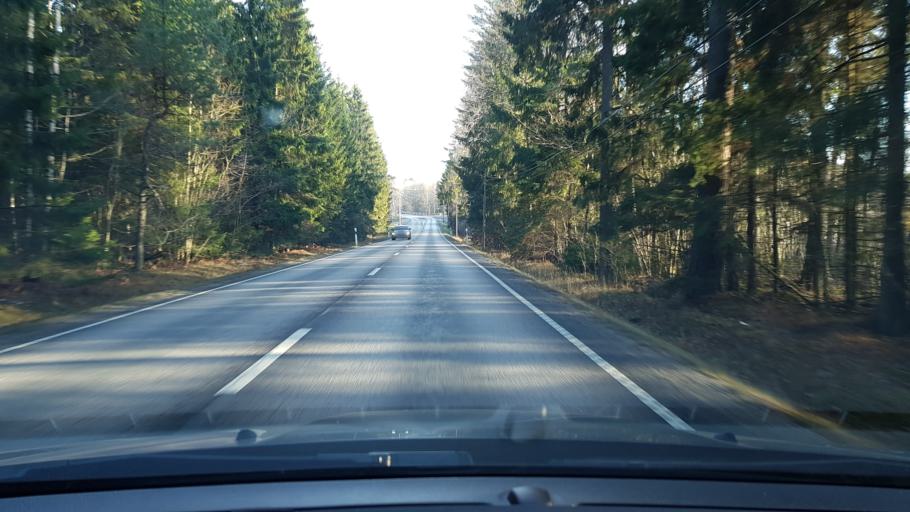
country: SE
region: Stockholm
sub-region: Norrtalje Kommun
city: Rimbo
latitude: 59.7399
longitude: 18.3276
